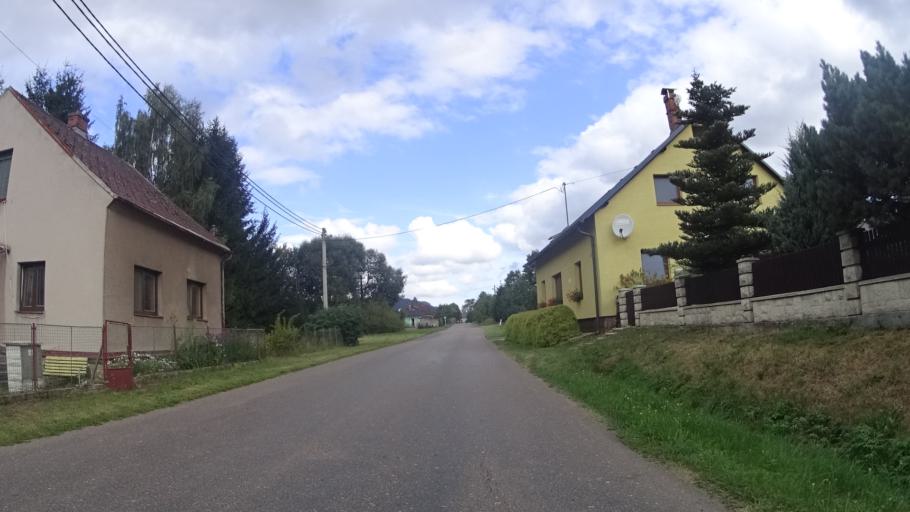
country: CZ
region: Pardubicky
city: Dolni Cermna
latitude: 49.9397
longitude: 16.5255
